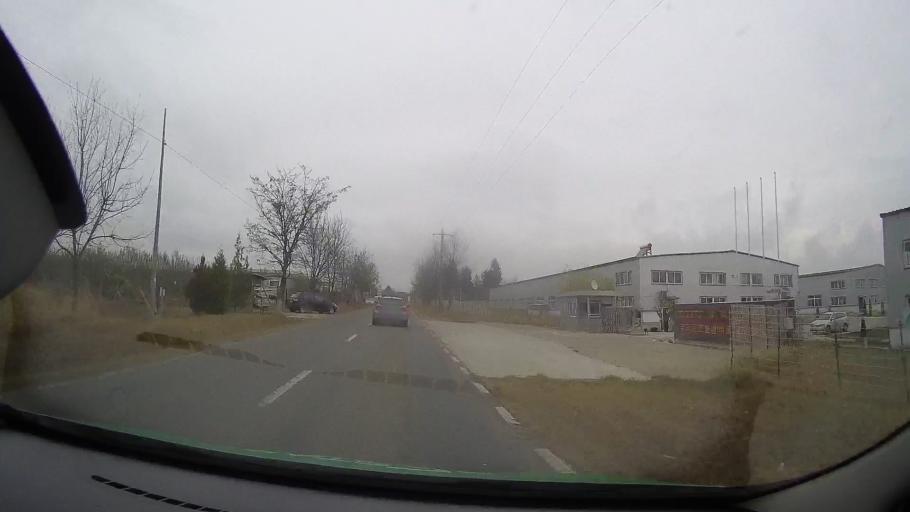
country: RO
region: Prahova
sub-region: Oras Baicoi
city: Liliesti
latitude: 45.0157
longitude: 25.8851
